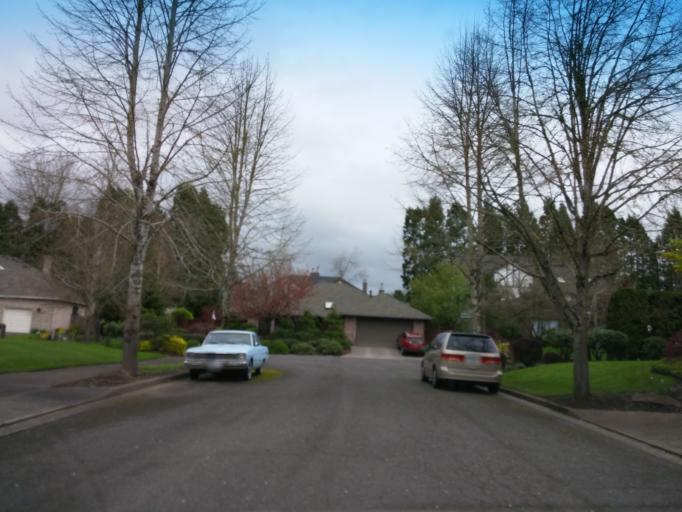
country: US
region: Oregon
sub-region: Washington County
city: Oak Hills
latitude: 45.5262
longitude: -122.8417
